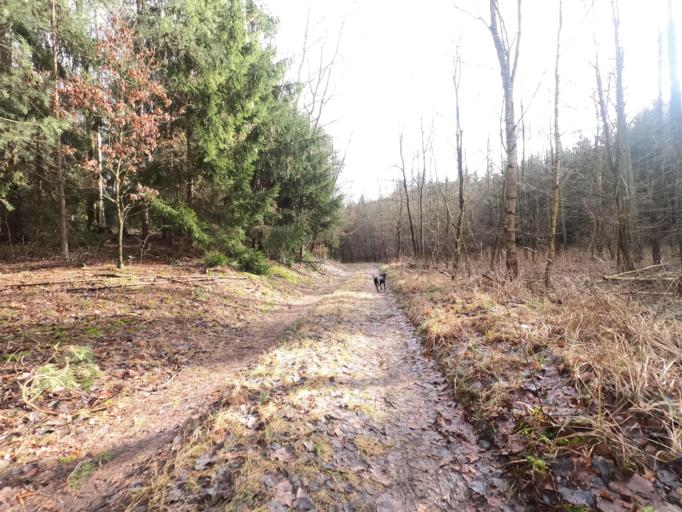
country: PL
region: Greater Poland Voivodeship
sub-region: Powiat pilski
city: Miasteczko Krajenskie
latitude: 53.1156
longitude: 16.9781
